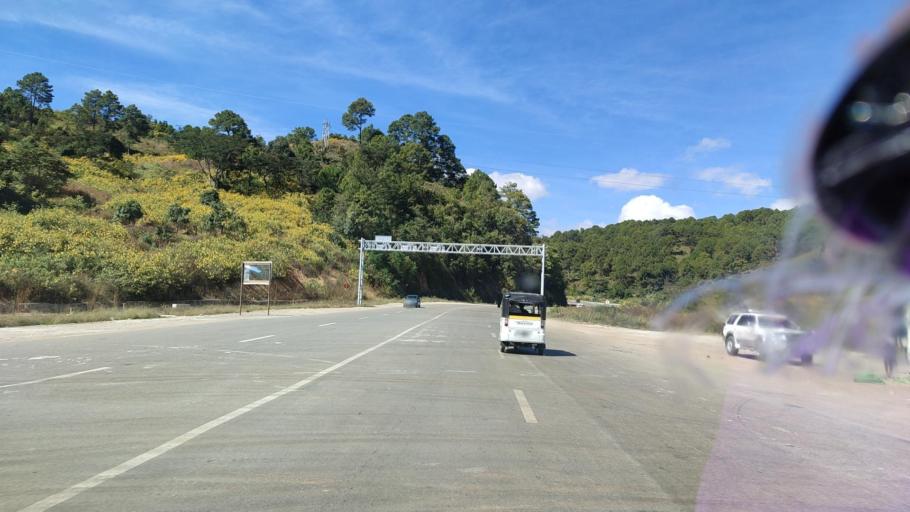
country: MM
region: Shan
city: Taunggyi
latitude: 20.6465
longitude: 96.6009
